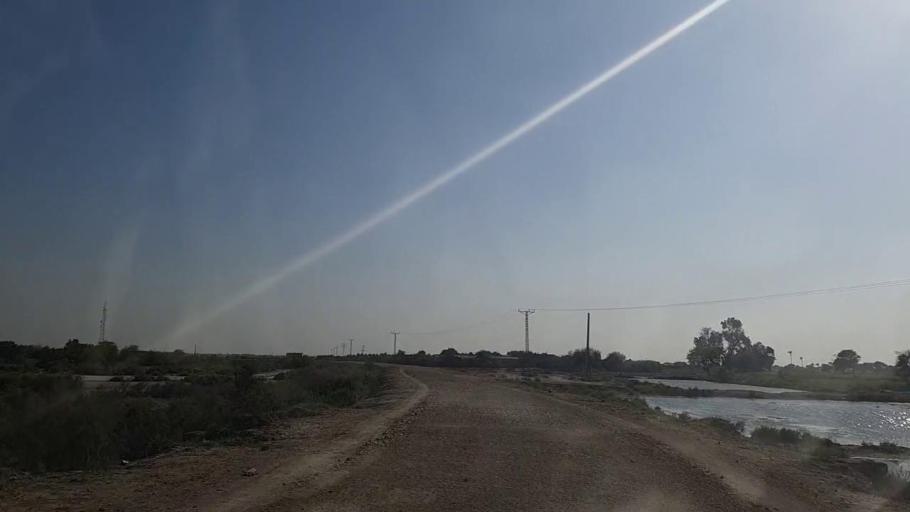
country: PK
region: Sindh
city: Mirpur Batoro
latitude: 24.5982
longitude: 68.1699
